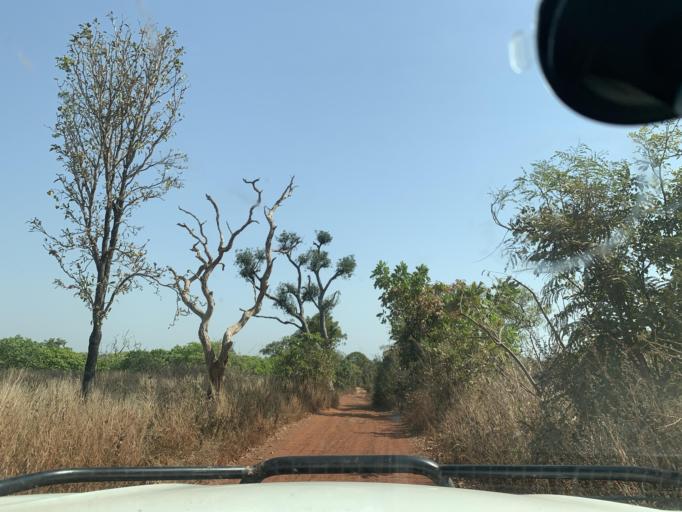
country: ML
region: Sikasso
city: Kolondieba
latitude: 10.8912
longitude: -6.7552
